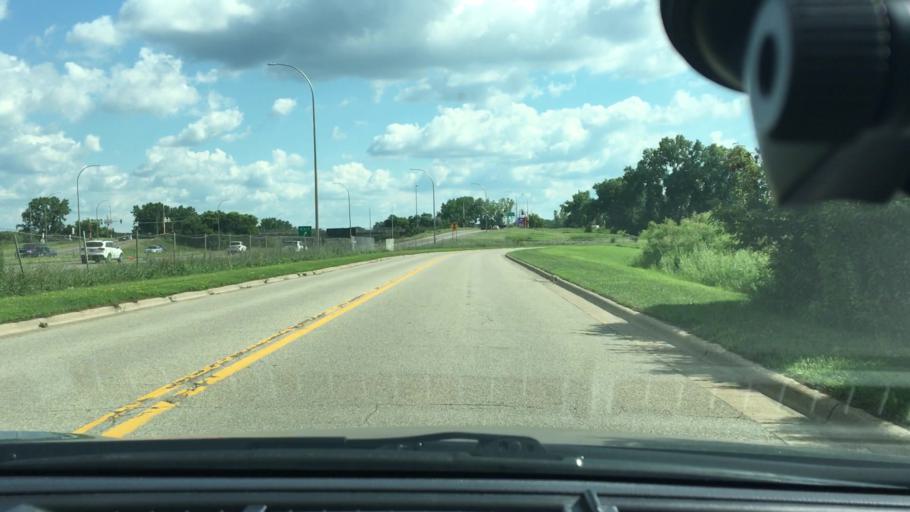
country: US
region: Minnesota
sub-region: Hennepin County
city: New Hope
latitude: 45.0466
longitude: -93.4013
